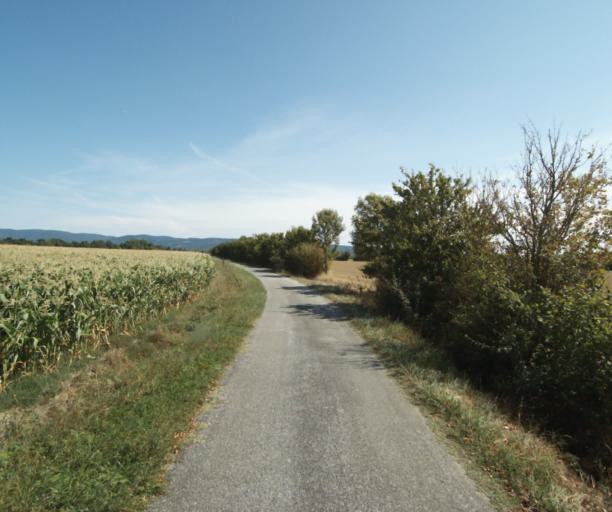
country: FR
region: Midi-Pyrenees
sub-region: Departement de la Haute-Garonne
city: Revel
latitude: 43.4867
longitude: 1.9737
